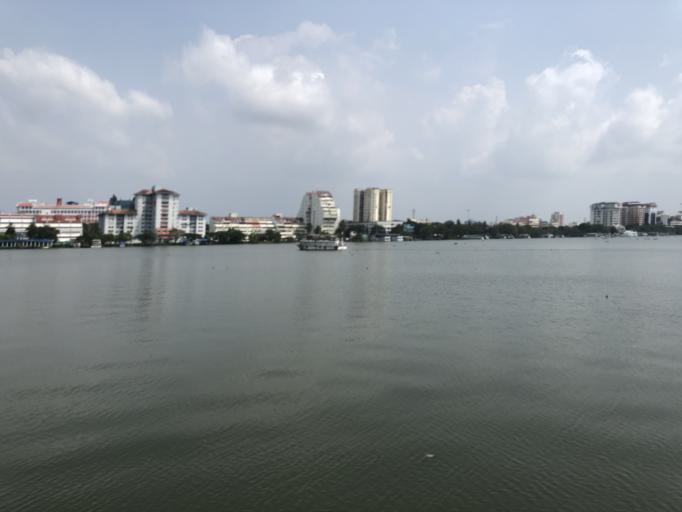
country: IN
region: Kerala
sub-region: Ernakulam
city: Cochin
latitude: 9.9841
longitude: 76.2684
